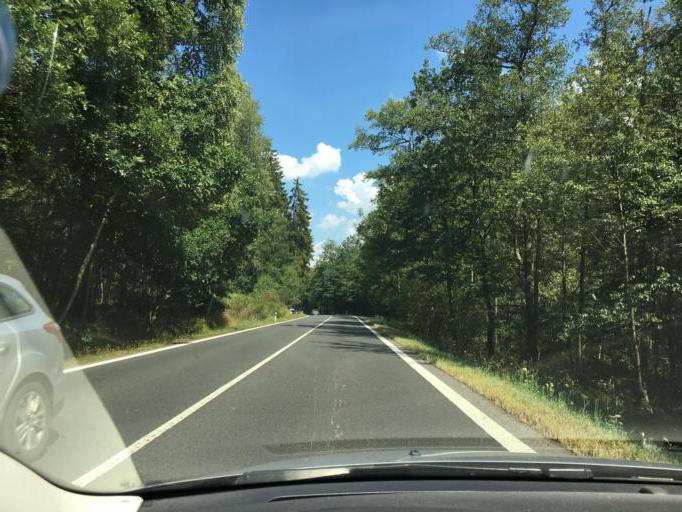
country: CZ
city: Brniste
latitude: 50.7732
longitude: 14.7095
